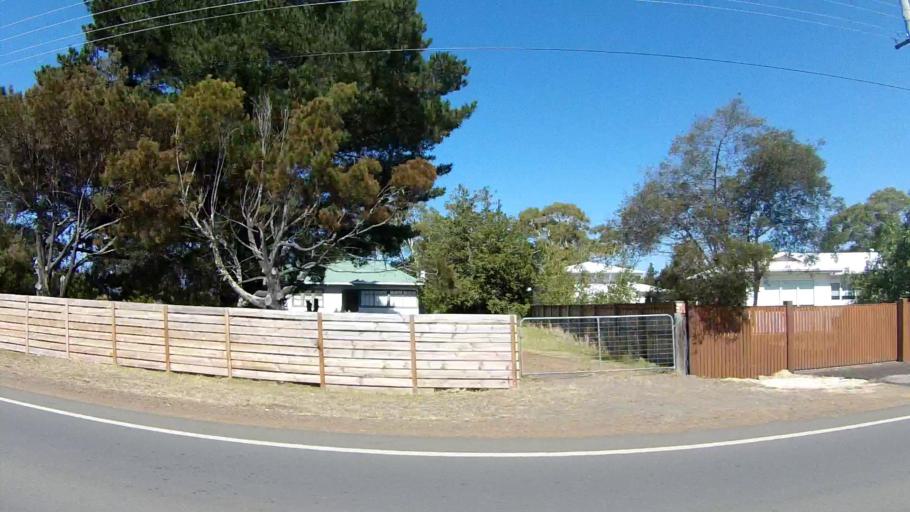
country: AU
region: Tasmania
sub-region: Sorell
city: Sorell
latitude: -42.5502
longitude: 147.8819
